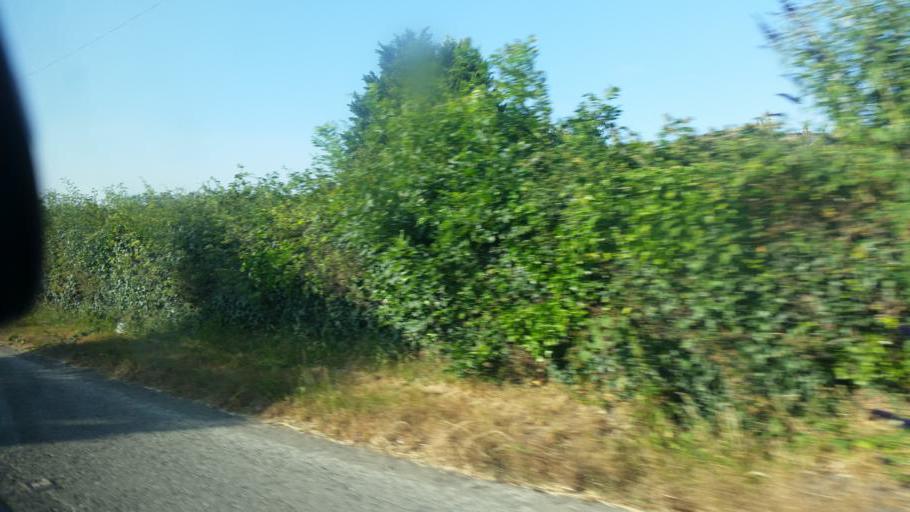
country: IE
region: Leinster
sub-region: An Mhi
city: Ashbourne
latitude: 53.4912
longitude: -6.3798
